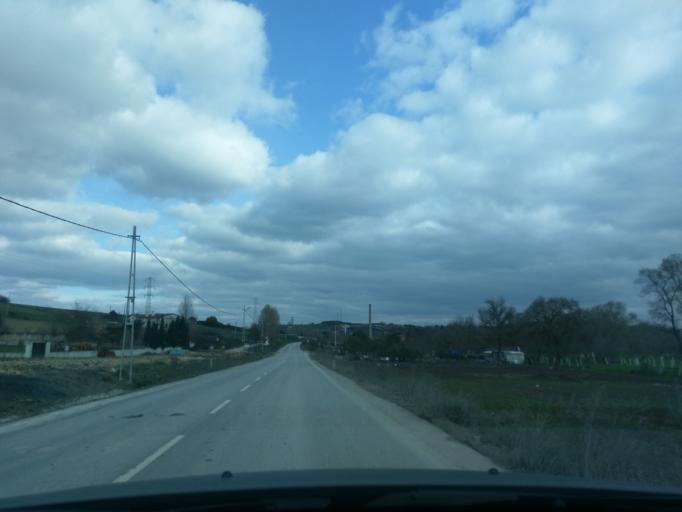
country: TR
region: Istanbul
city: Durusu
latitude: 41.2946
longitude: 28.6676
